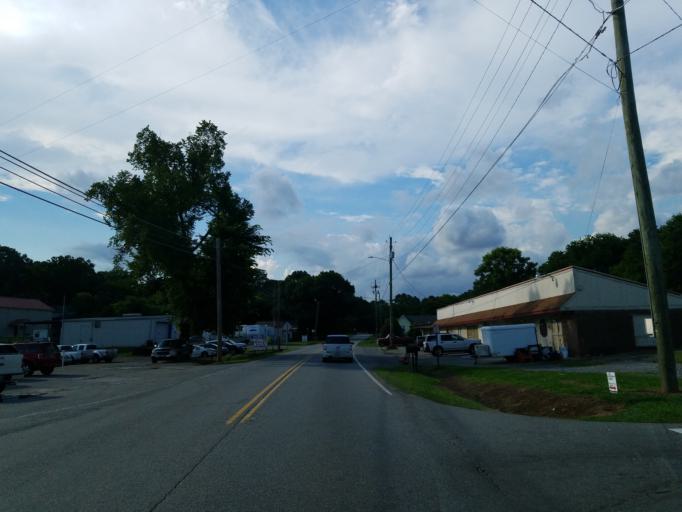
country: US
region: Georgia
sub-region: Bartow County
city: Emerson
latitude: 34.1270
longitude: -84.7566
